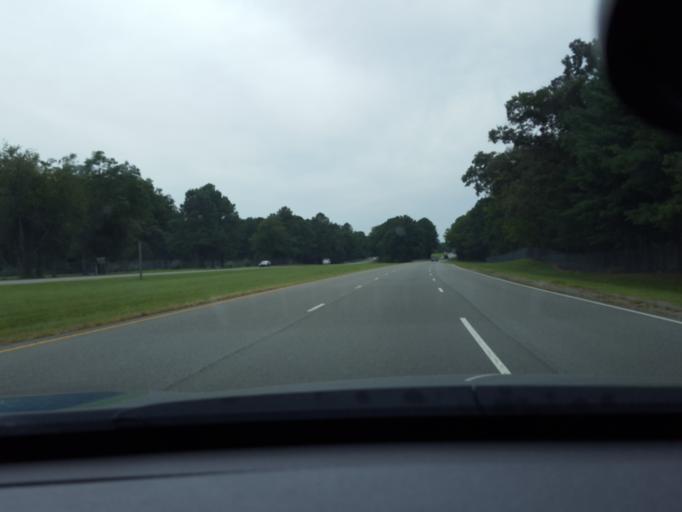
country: US
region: Virginia
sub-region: Caroline County
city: Bowling Green
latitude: 38.0715
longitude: -77.3222
